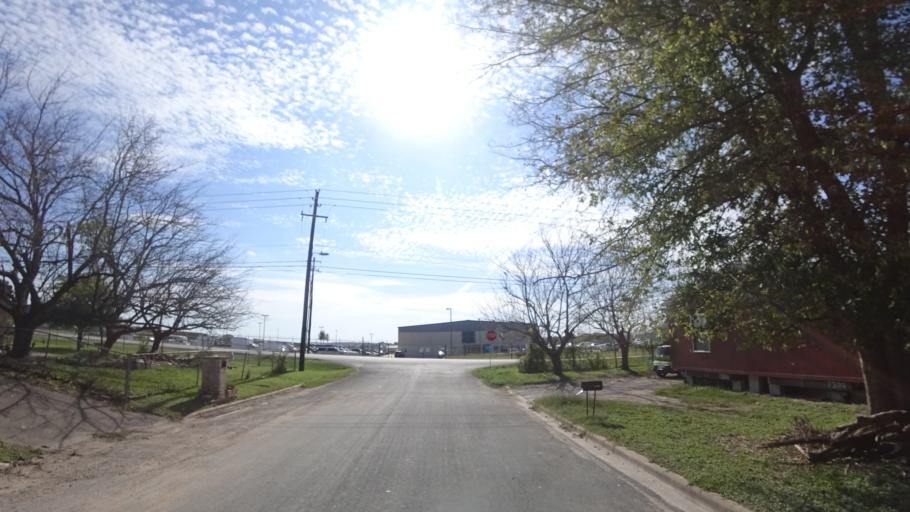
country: US
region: Texas
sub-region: Travis County
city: Pflugerville
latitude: 30.4070
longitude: -97.6306
